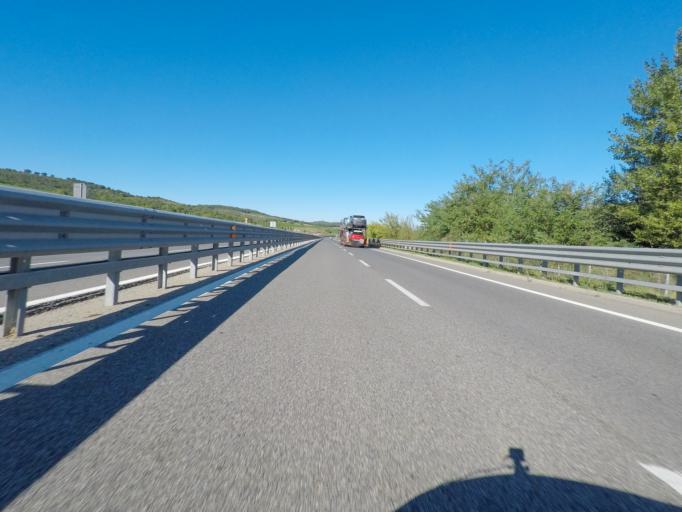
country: IT
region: Tuscany
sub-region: Provincia di Grosseto
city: Campagnatico
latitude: 42.8974
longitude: 11.2390
